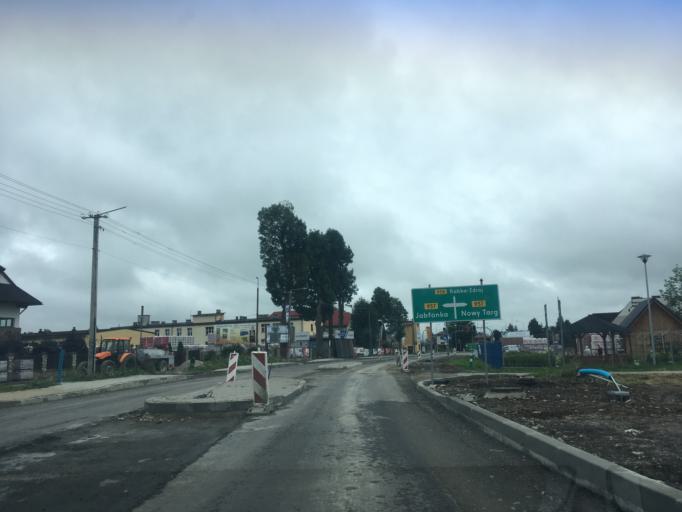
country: PL
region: Lesser Poland Voivodeship
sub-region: Powiat nowotarski
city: Czarny Dunajec
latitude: 49.4406
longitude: 19.8493
